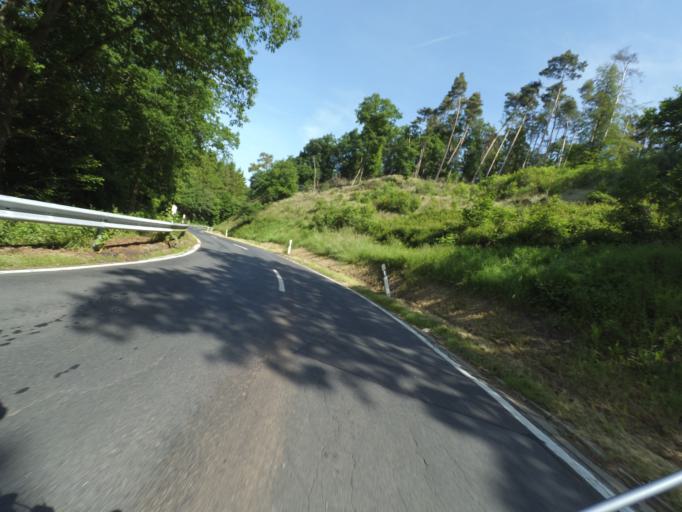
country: DE
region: Rheinland-Pfalz
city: Landkern
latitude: 50.2165
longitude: 7.1527
